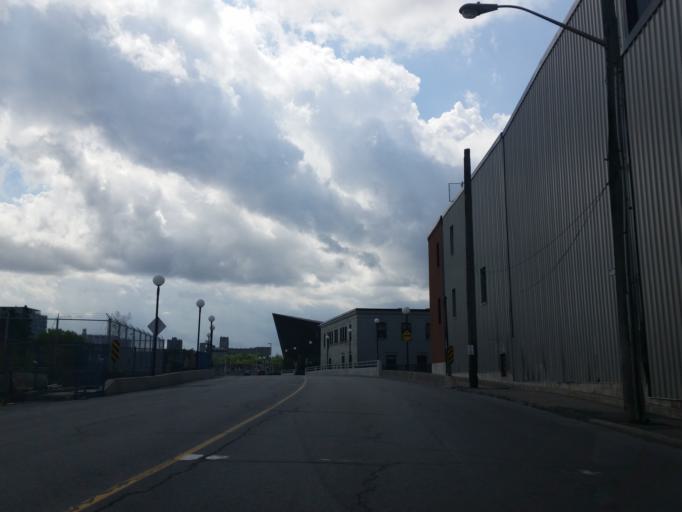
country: CA
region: Ontario
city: Ottawa
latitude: 45.4202
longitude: -75.7177
